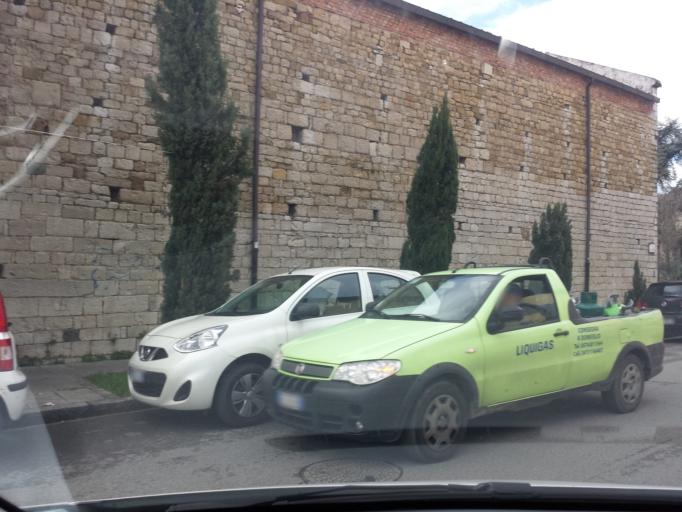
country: IT
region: Tuscany
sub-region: Provincia di Prato
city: Prato
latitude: 43.8886
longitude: 11.0571
